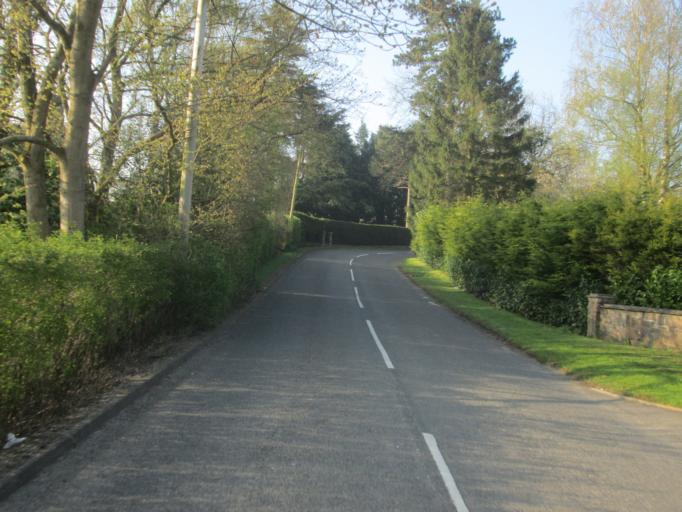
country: GB
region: England
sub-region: Derbyshire
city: Wirksworth
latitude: 53.0236
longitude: -1.5649
